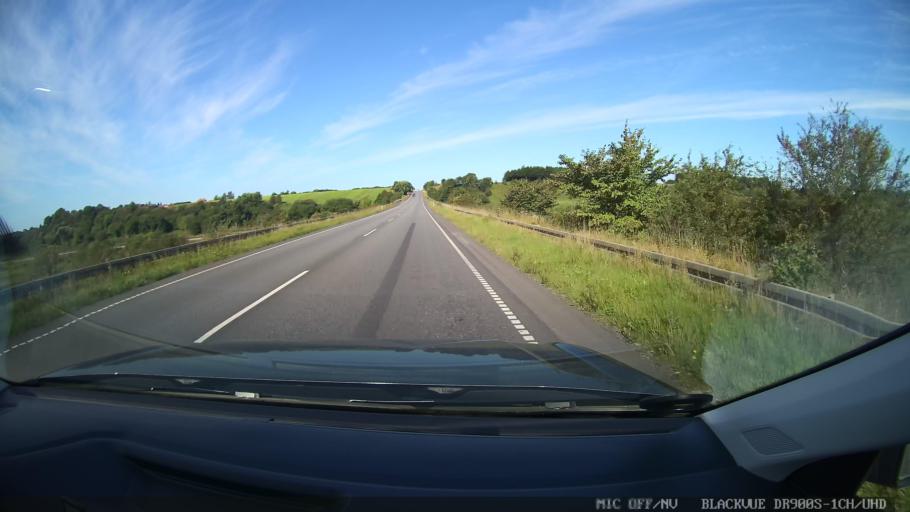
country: DK
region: North Denmark
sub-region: Mariagerfjord Kommune
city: Hobro
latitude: 56.6577
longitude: 9.7894
